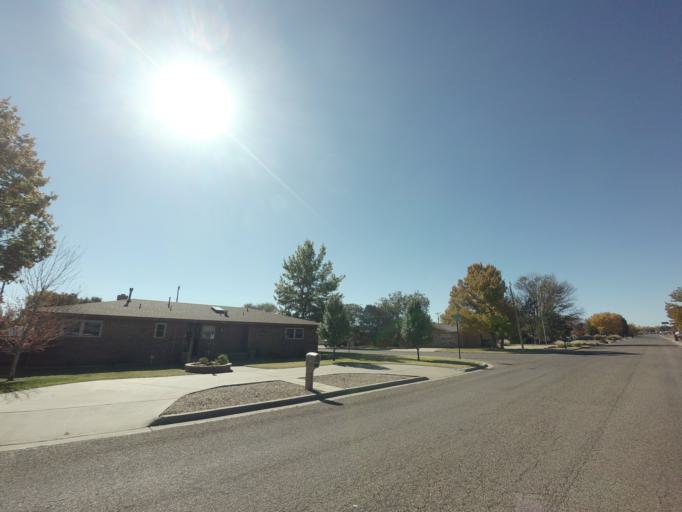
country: US
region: New Mexico
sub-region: Curry County
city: Clovis
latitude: 34.4216
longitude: -103.1913
